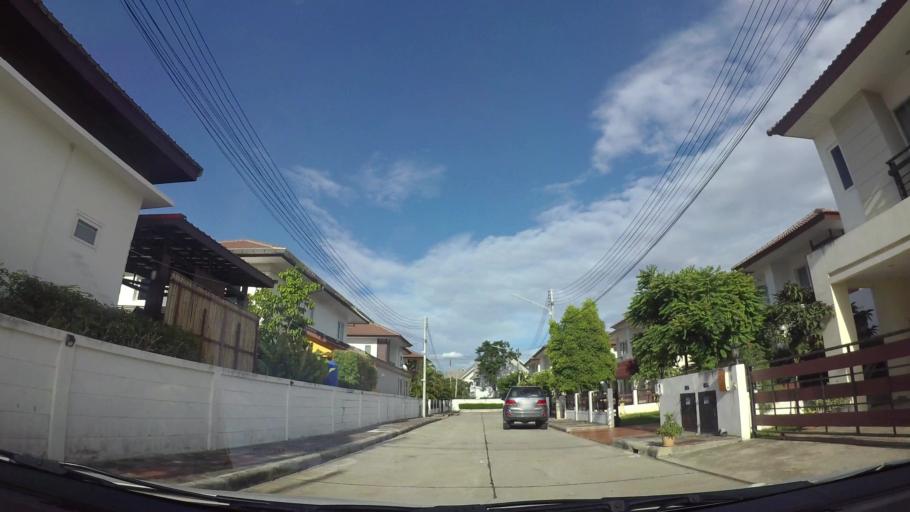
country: TH
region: Chiang Mai
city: Saraphi
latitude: 18.7521
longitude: 99.0262
